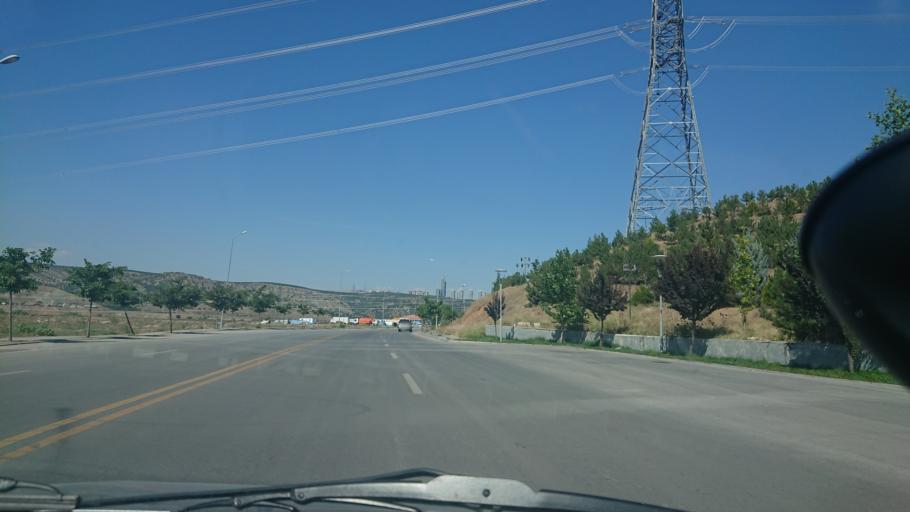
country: TR
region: Ankara
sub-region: Goelbasi
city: Golbasi
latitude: 39.8038
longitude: 32.8141
